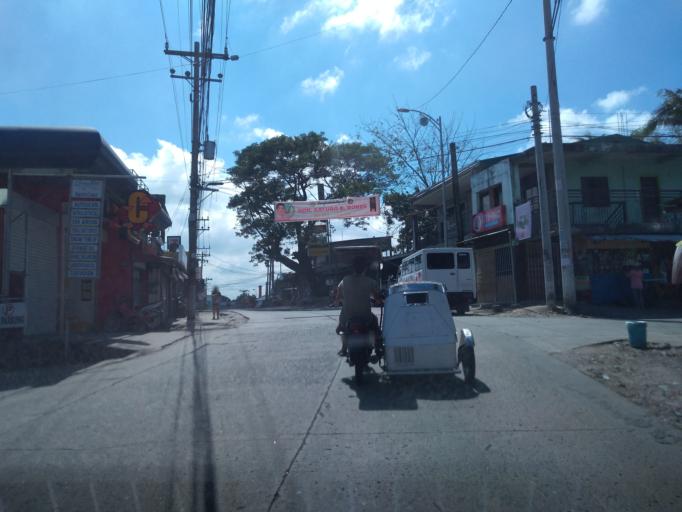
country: PH
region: Central Luzon
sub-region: Province of Bulacan
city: Bitungol
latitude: 14.8545
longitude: 121.0725
